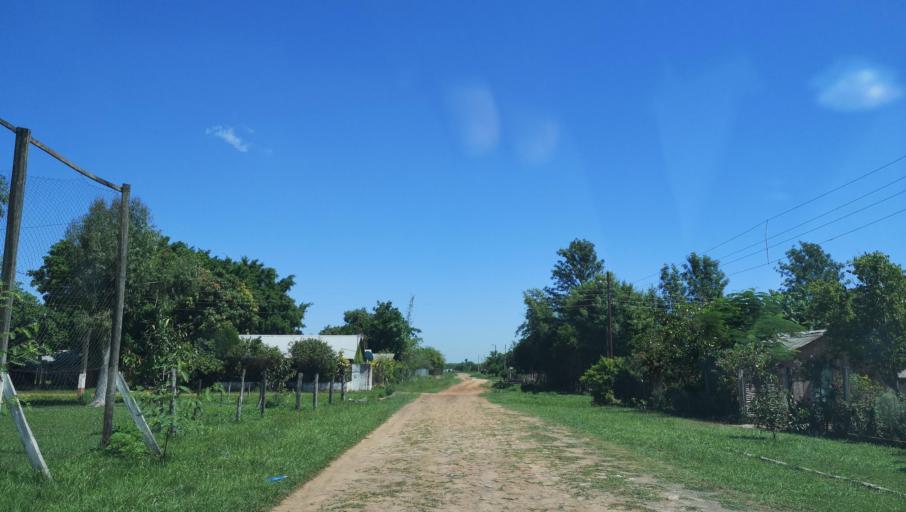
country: PY
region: Caaguazu
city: Carayao
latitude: -25.1924
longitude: -56.4022
